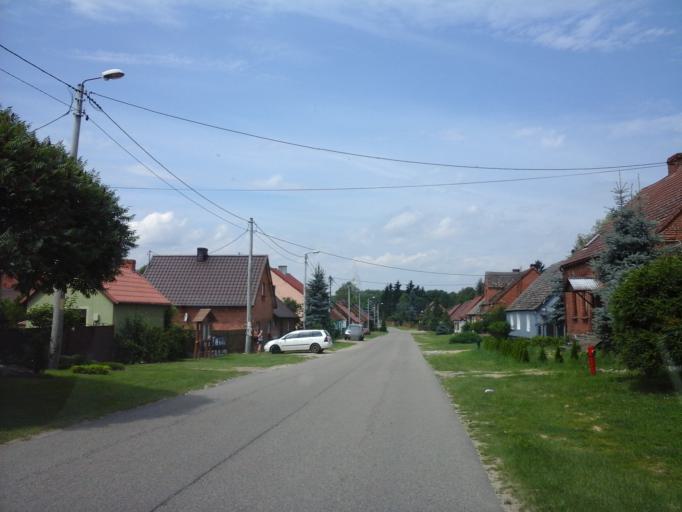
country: PL
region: West Pomeranian Voivodeship
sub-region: Powiat choszczenski
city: Bierzwnik
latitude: 53.0408
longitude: 15.6468
